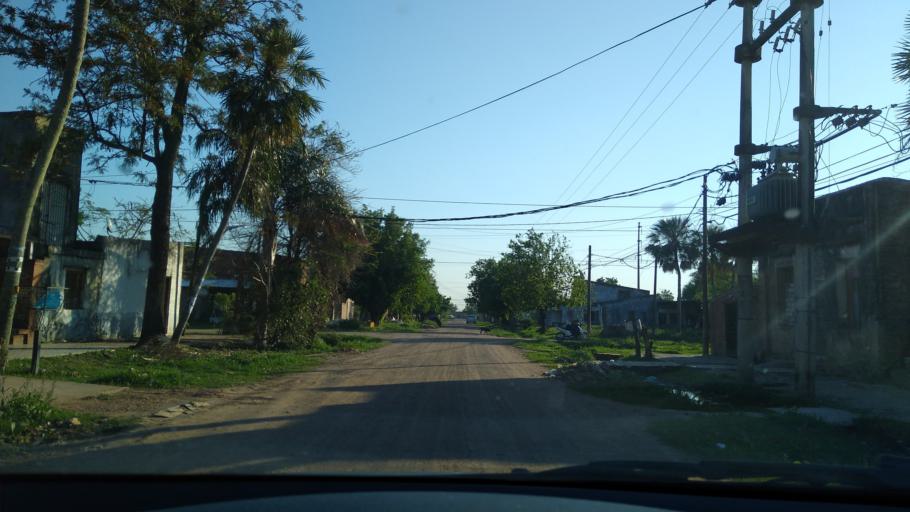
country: AR
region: Chaco
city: Barranqueras
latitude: -27.4914
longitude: -58.9331
